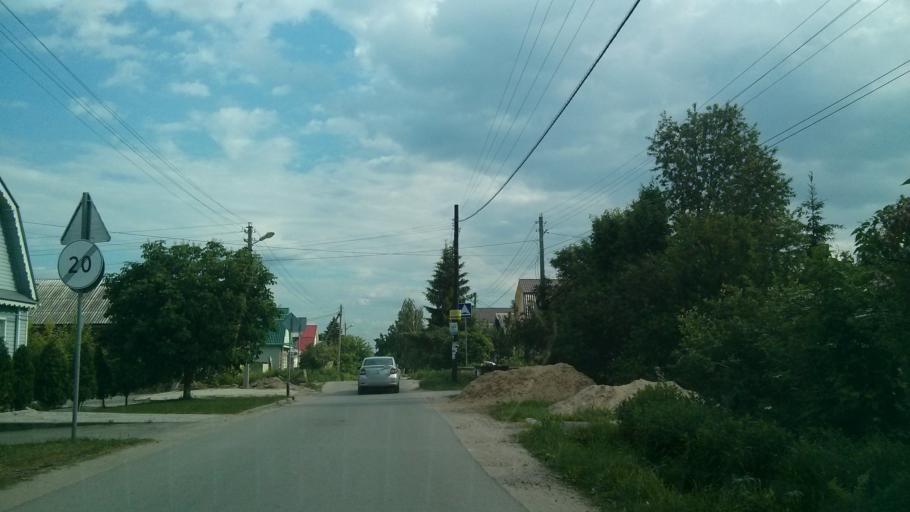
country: RU
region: Nizjnij Novgorod
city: Afonino
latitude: 56.2860
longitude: 44.1003
